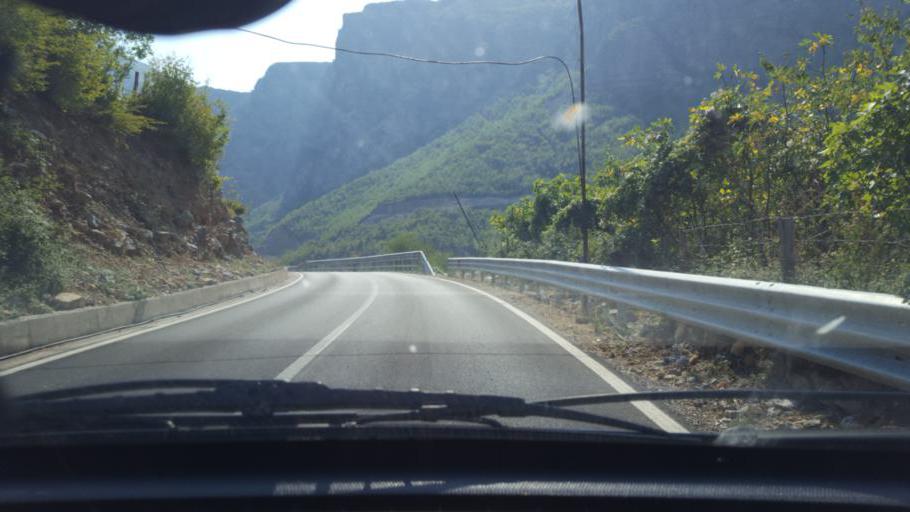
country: AL
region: Shkoder
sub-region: Rrethi i Malesia e Madhe
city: Kastrat
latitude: 42.4186
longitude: 19.5103
